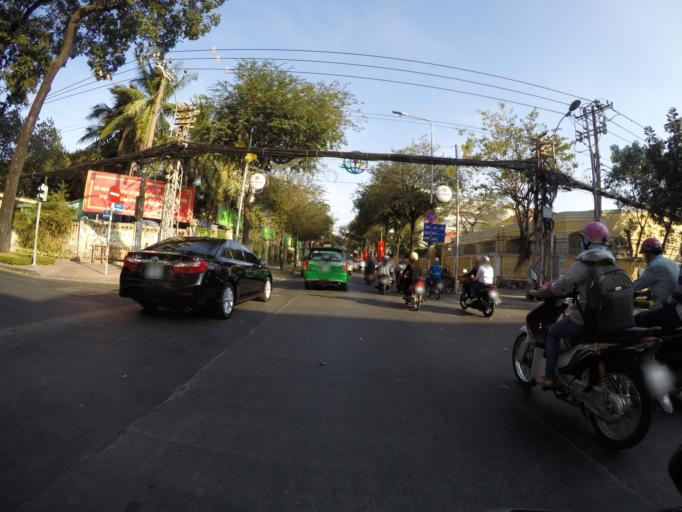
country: VN
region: Ho Chi Minh City
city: Quan Mot
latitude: 10.7814
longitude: 106.6928
